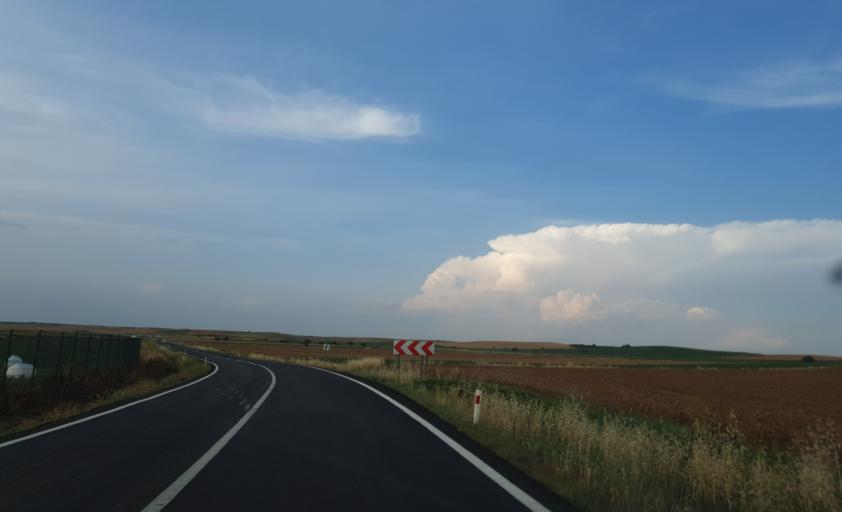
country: TR
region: Tekirdag
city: Hayrabolu
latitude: 41.2389
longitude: 27.1323
